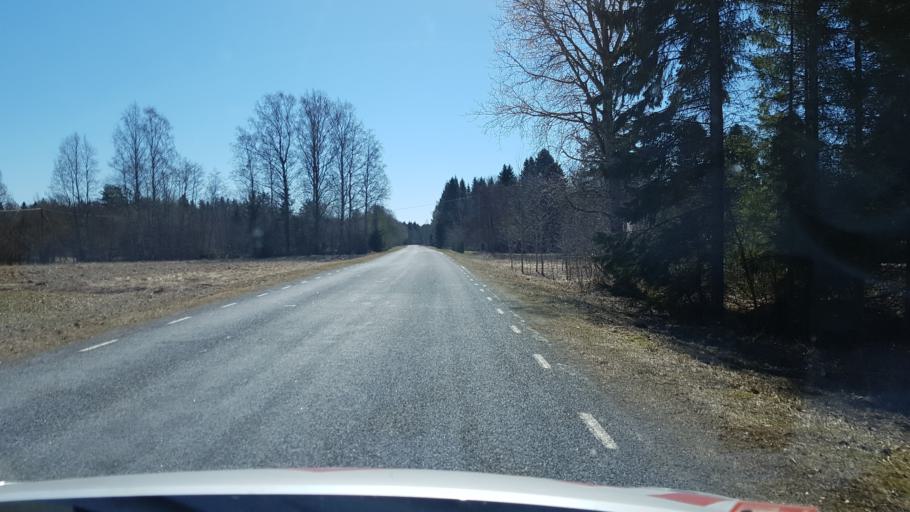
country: EE
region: Laeaene-Virumaa
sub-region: Haljala vald
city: Haljala
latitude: 59.5124
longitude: 26.2323
